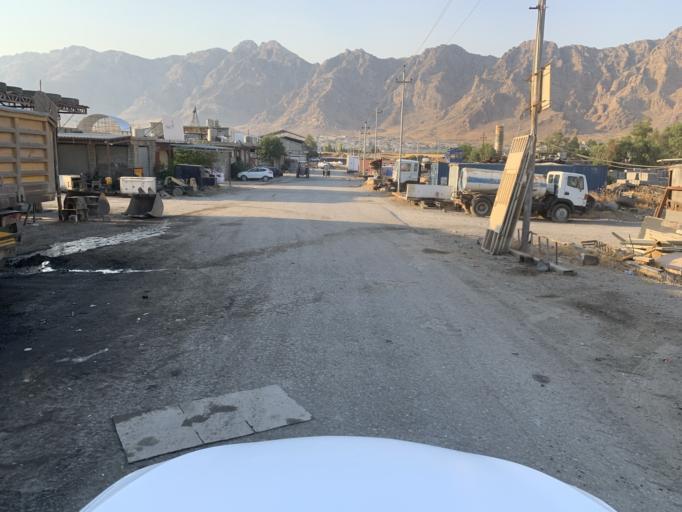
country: IQ
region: As Sulaymaniyah
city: Raniye
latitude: 36.2457
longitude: 44.8889
